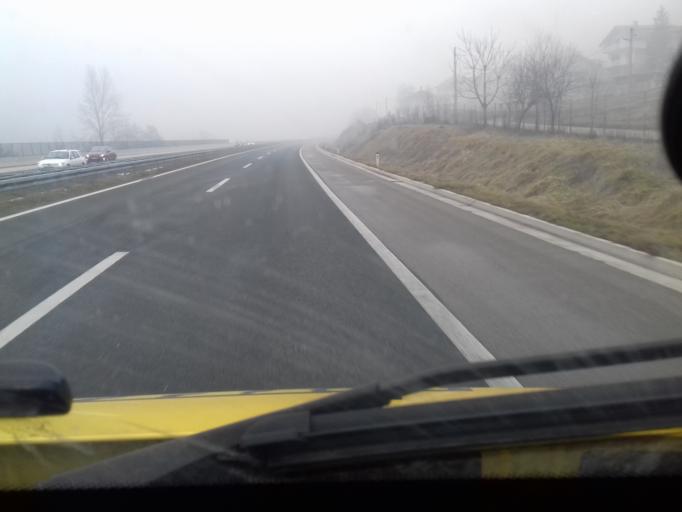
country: BA
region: Federation of Bosnia and Herzegovina
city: Dobrinje
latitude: 44.0730
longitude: 18.1075
